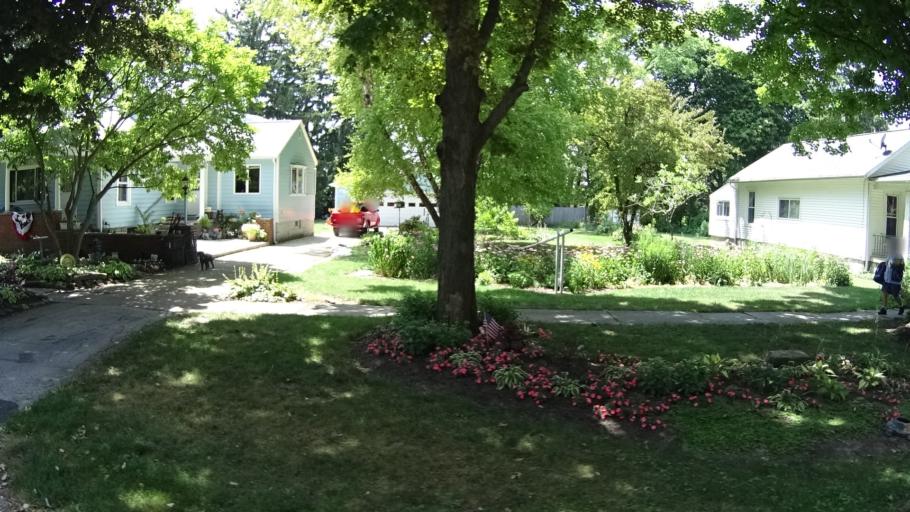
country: US
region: Ohio
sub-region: Erie County
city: Sandusky
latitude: 41.4429
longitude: -82.7020
